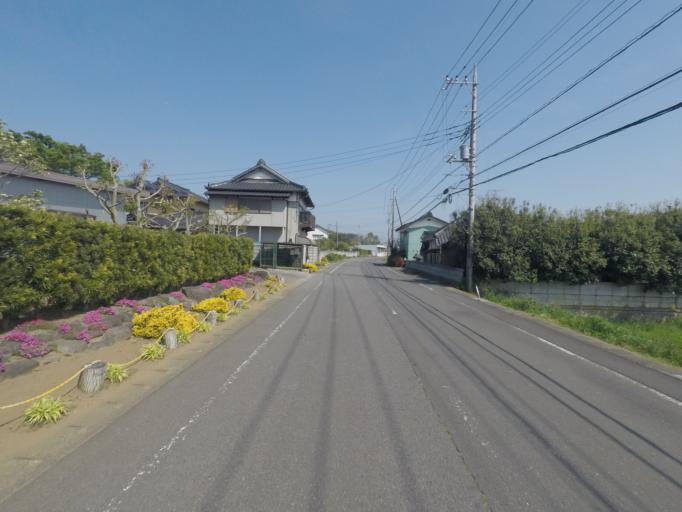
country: JP
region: Ibaraki
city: Inashiki
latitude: 36.0700
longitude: 140.3152
